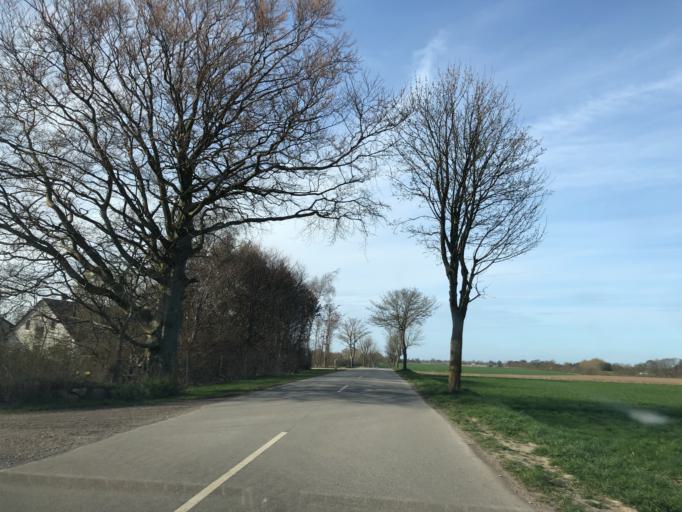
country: DK
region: Zealand
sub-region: Stevns Kommune
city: Store Heddinge
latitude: 55.3059
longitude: 12.4379
